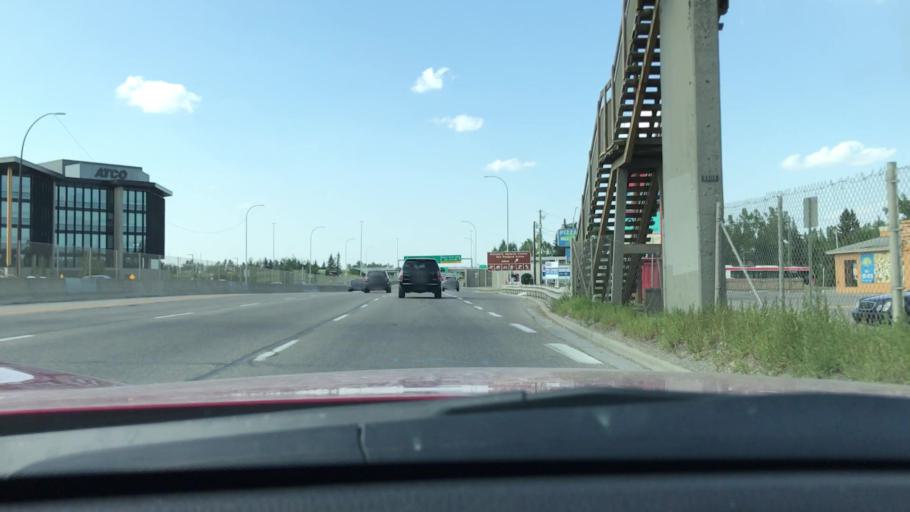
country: CA
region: Alberta
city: Calgary
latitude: 51.0043
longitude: -114.1178
